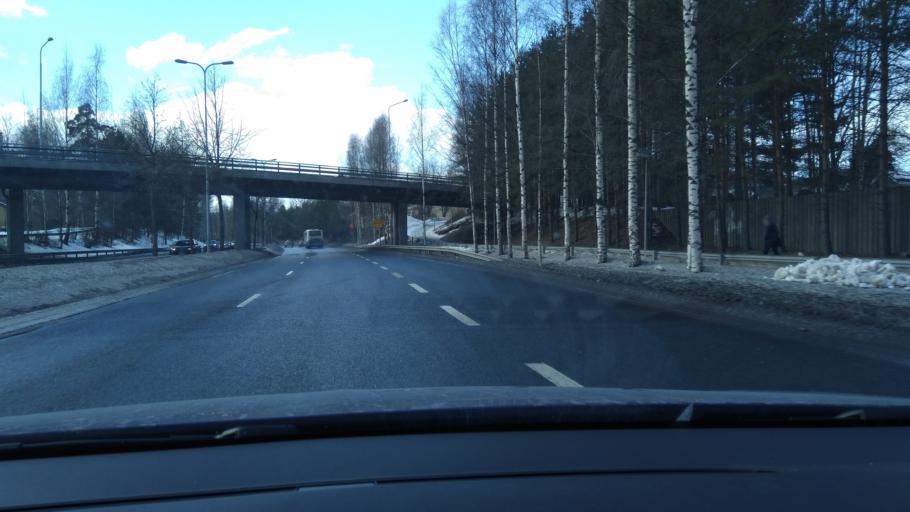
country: FI
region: Pirkanmaa
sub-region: Tampere
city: Tampere
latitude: 61.5037
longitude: 23.8030
